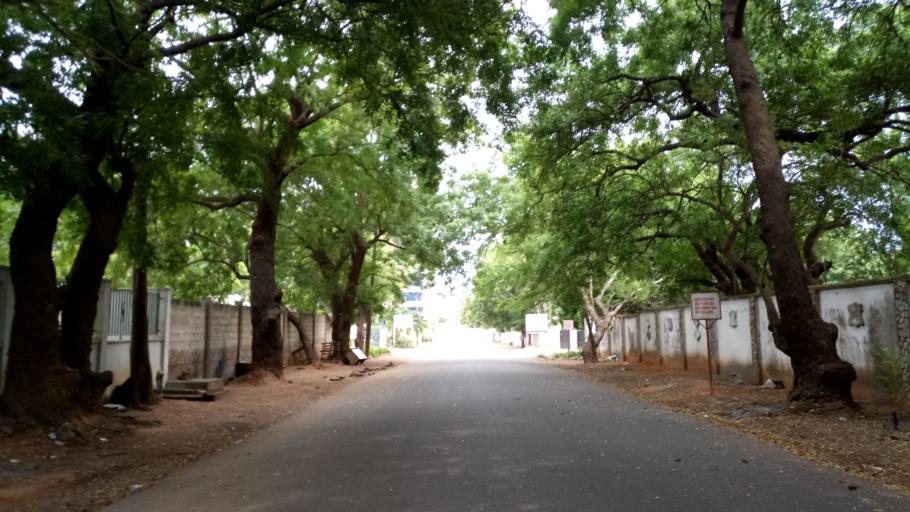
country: GH
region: Greater Accra
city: Accra
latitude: 5.5584
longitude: -0.1944
